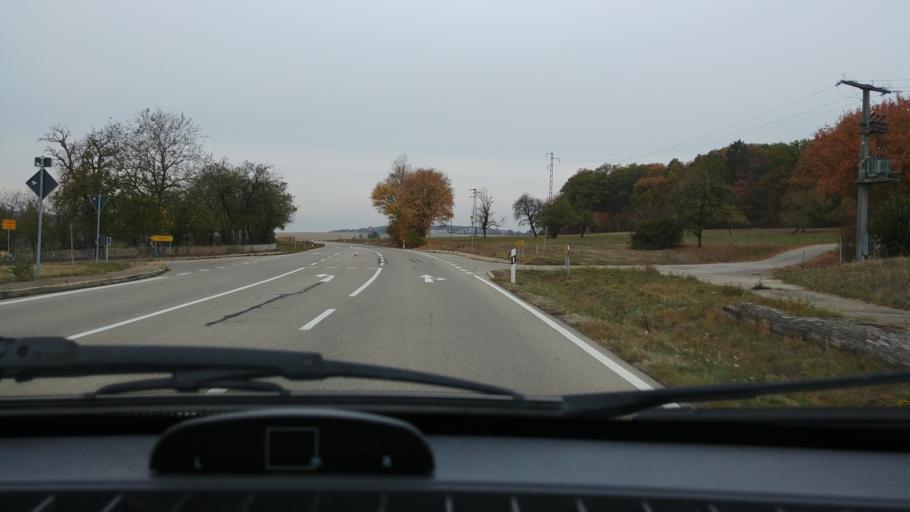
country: DE
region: Baden-Wuerttemberg
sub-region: Regierungsbezirk Stuttgart
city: Niederstetten
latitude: 49.3649
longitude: 9.8974
